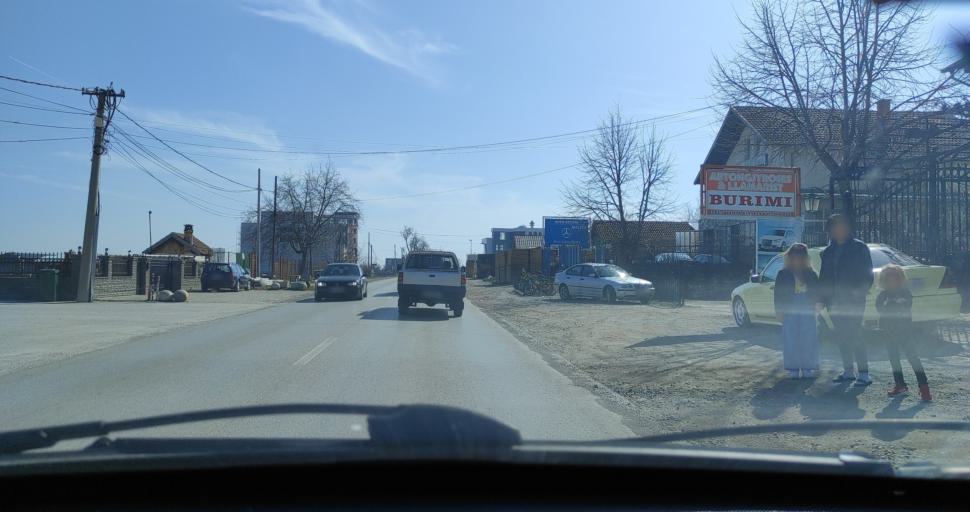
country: XK
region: Pec
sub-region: Komuna e Pejes
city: Peje
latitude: 42.6368
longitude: 20.2992
